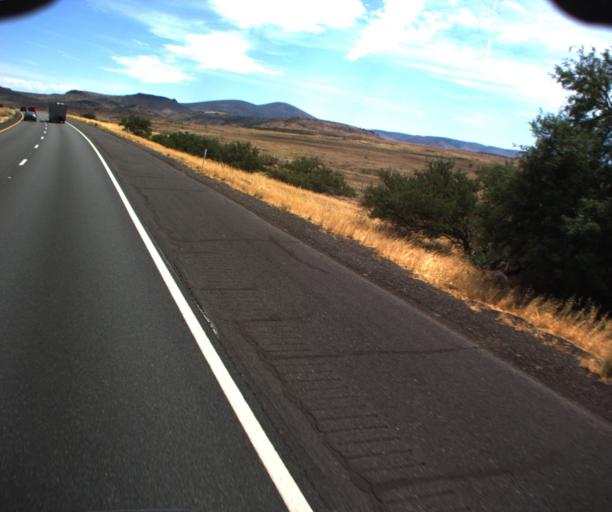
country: US
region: Arizona
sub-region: Yavapai County
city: Cordes Lakes
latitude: 34.4268
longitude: -112.0386
